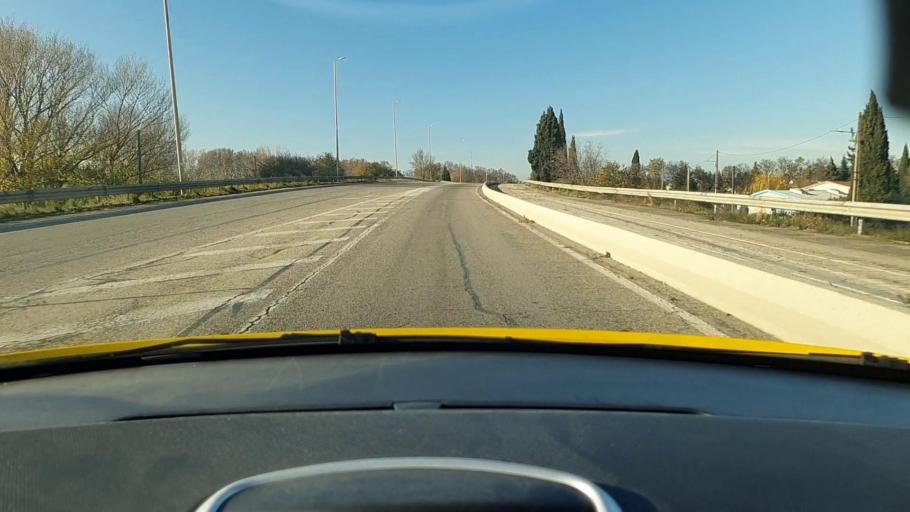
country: FR
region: Languedoc-Roussillon
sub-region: Departement du Gard
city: Caissargues
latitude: 43.8218
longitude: 4.3837
